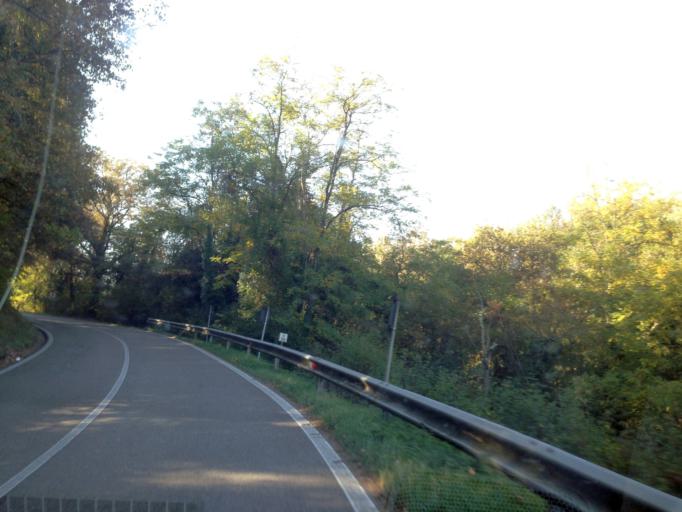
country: IT
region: Tuscany
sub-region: Province of Florence
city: Panzano in Chianti
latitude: 43.5158
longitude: 11.2917
